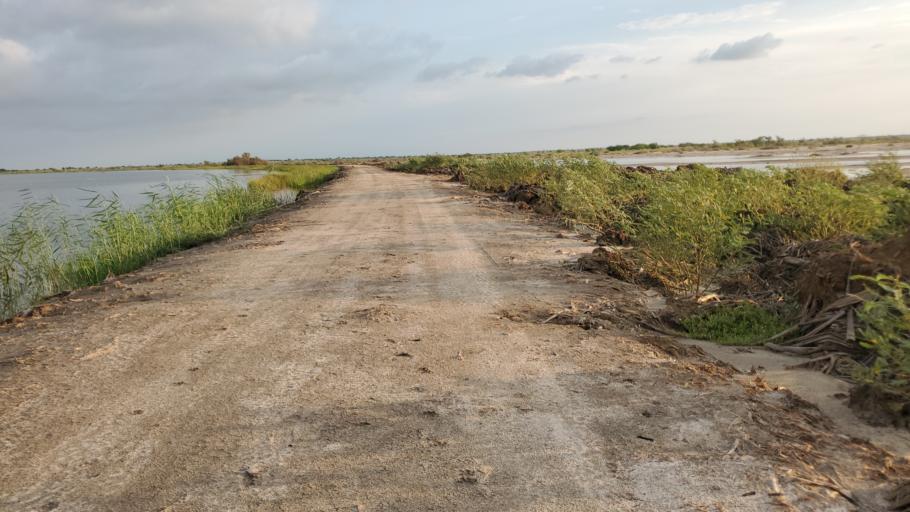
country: SN
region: Saint-Louis
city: Saint-Louis
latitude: 16.0272
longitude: -16.4104
